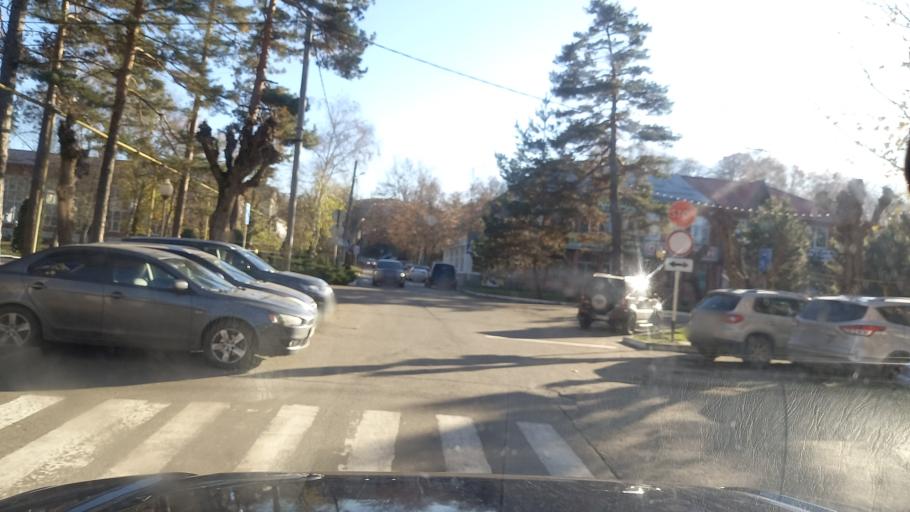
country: RU
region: Krasnodarskiy
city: Goryachiy Klyuch
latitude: 44.6269
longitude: 39.1053
